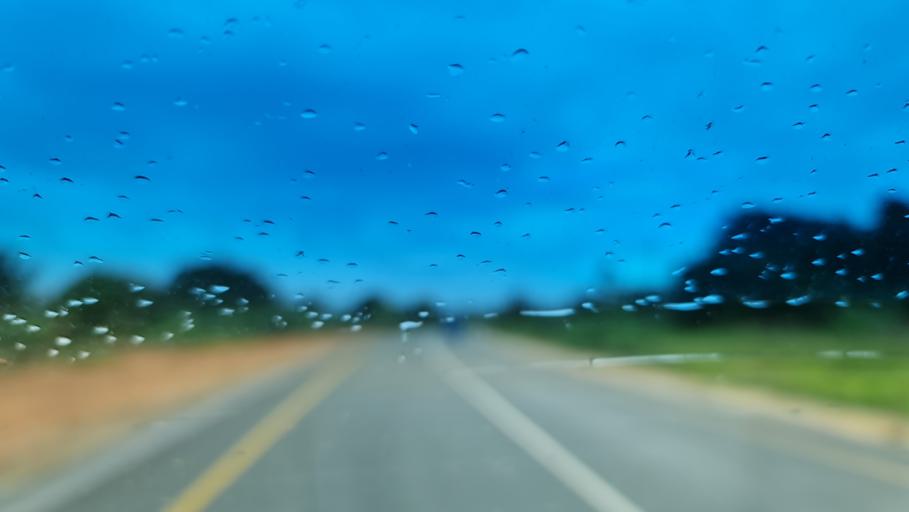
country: MZ
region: Nampula
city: Nampula
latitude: -15.5341
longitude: 39.3309
